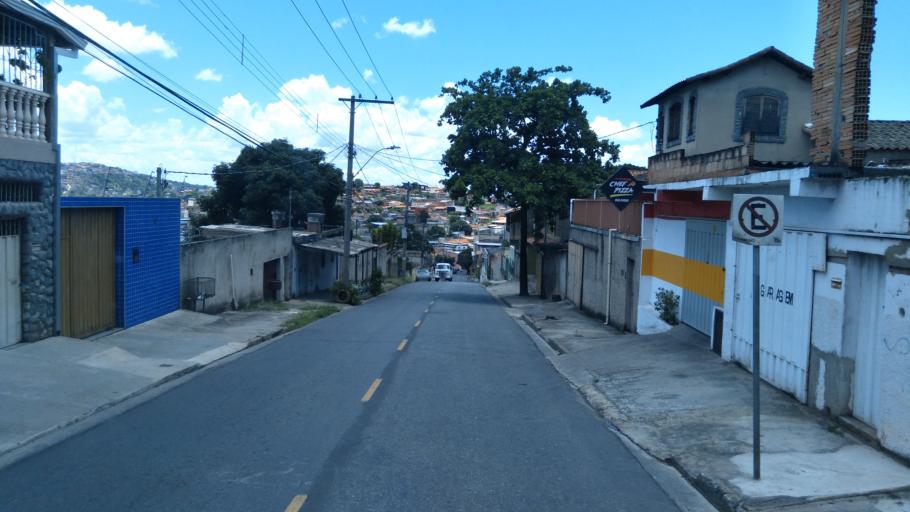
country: BR
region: Minas Gerais
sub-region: Belo Horizonte
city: Belo Horizonte
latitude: -19.8539
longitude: -43.8972
